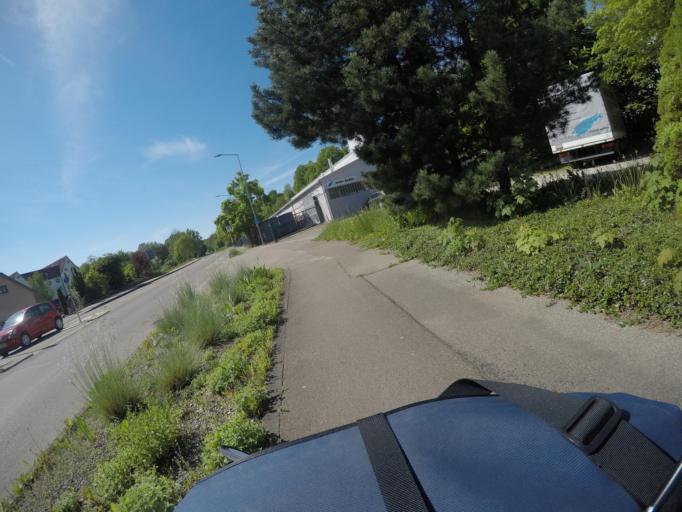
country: DE
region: Baden-Wuerttemberg
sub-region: Regierungsbezirk Stuttgart
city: Huttlingen
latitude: 48.8659
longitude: 10.0980
